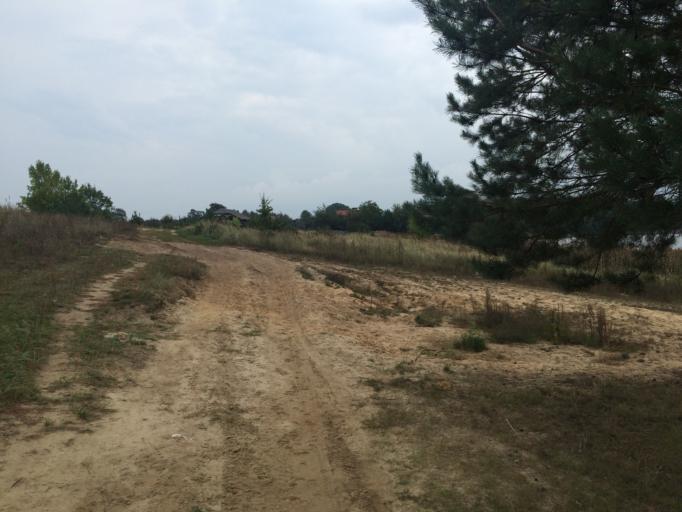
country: PL
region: Swietokrzyskie
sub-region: Powiat starachowicki
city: Starachowice
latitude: 51.0270
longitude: 21.0486
